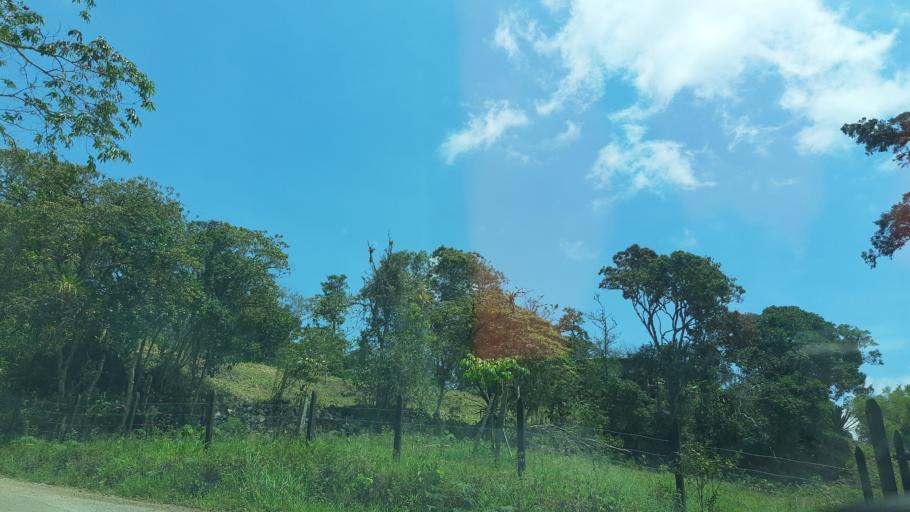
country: CO
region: Boyaca
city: Chinavita
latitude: 5.1270
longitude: -73.3822
